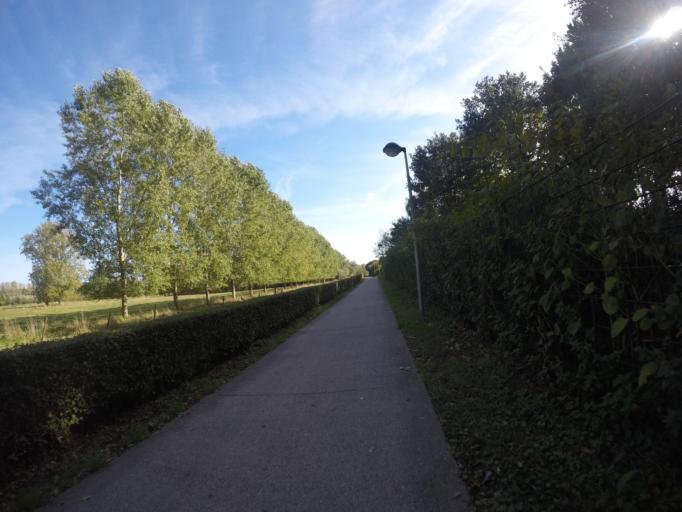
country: BE
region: Flanders
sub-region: Provincie Limburg
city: Diepenbeek
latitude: 50.9122
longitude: 5.4275
